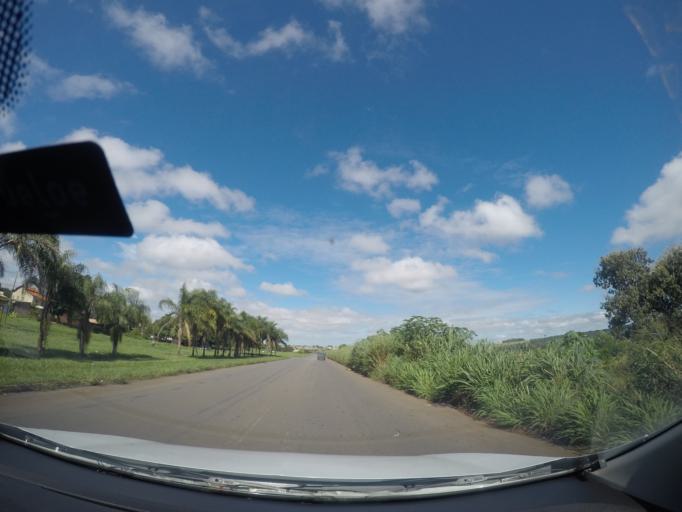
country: BR
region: Goias
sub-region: Senador Canedo
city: Senador Canedo
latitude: -16.6492
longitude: -49.1576
